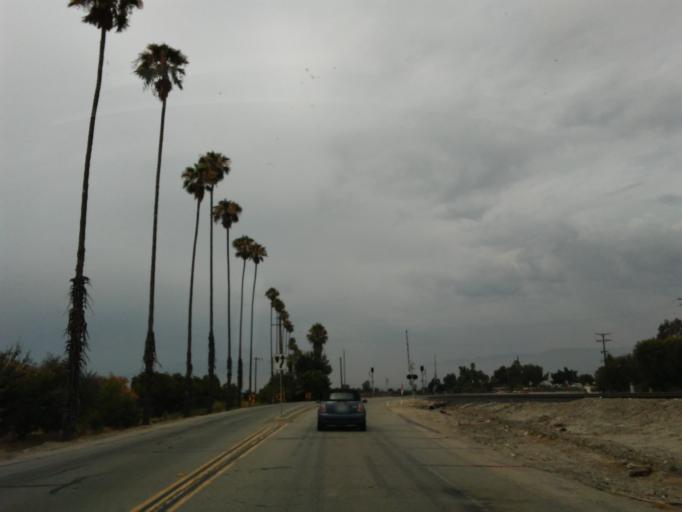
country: US
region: California
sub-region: San Bernardino County
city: Redlands
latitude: 34.0304
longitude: -117.2077
